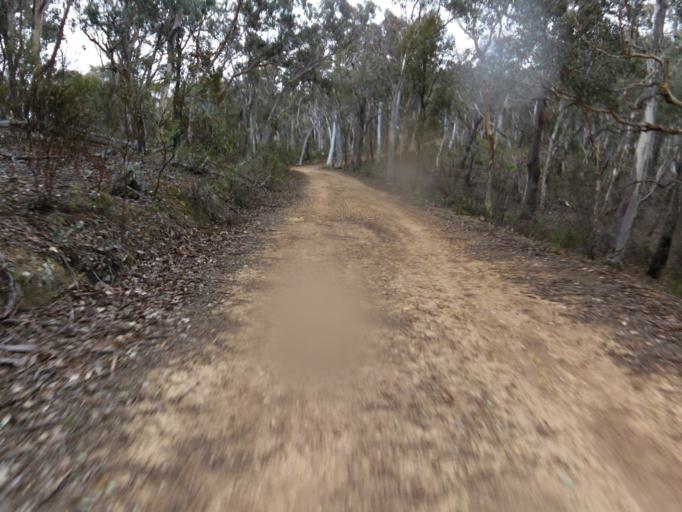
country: AU
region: Australian Capital Territory
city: Acton
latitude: -35.2687
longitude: 149.0990
